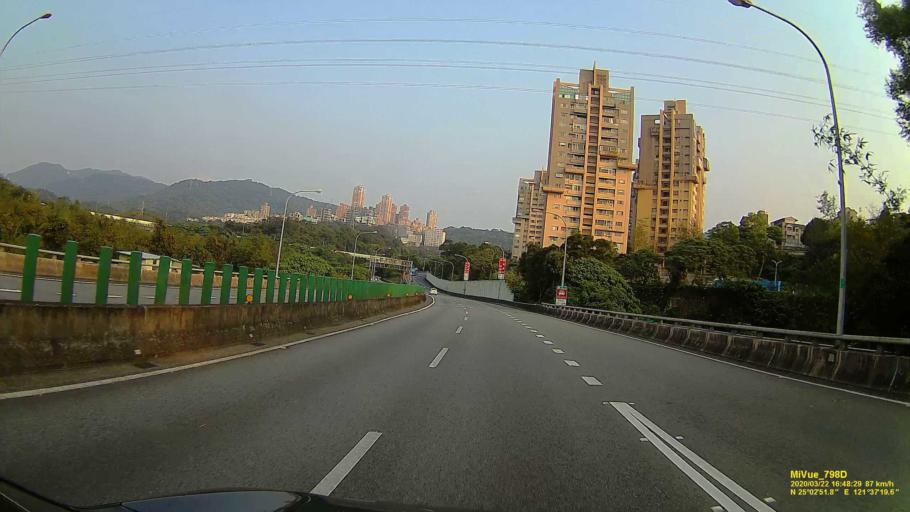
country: TW
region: Taipei
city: Taipei
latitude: 25.0473
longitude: 121.6223
